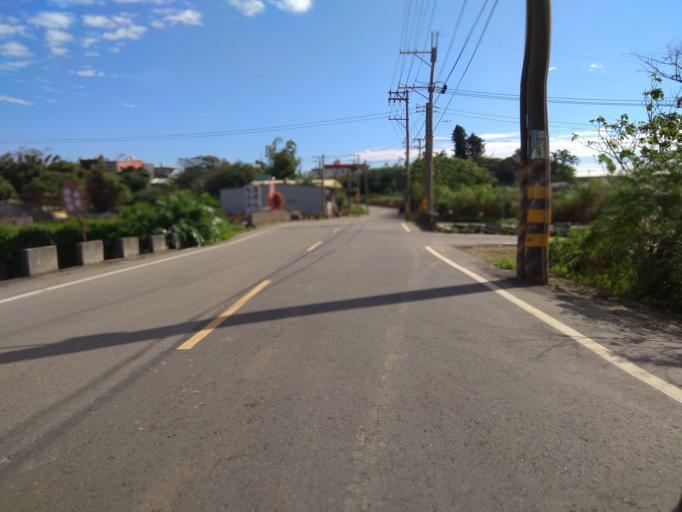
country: TW
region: Taiwan
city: Taoyuan City
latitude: 25.0397
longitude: 121.1269
